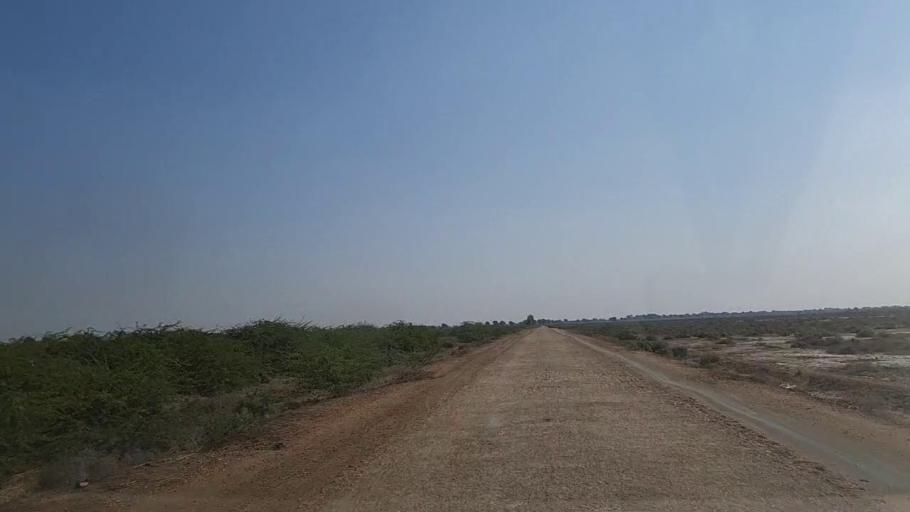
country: PK
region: Sindh
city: Digri
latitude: 25.1648
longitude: 69.1702
